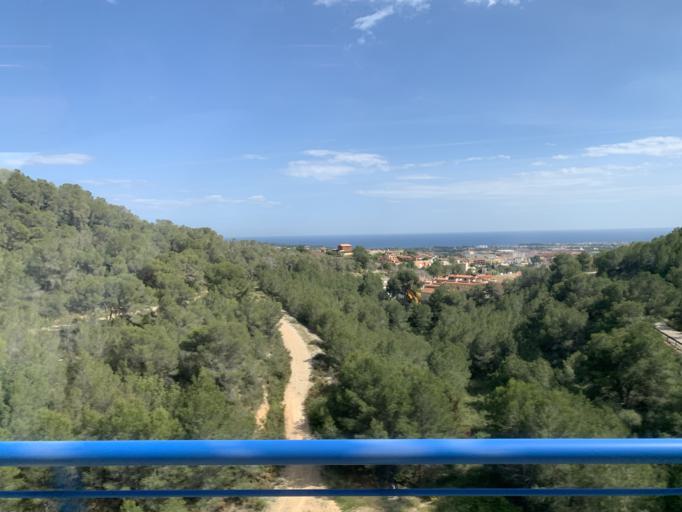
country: ES
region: Catalonia
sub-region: Provincia de Tarragona
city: Roda de Bara
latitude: 41.1948
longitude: 1.4563
